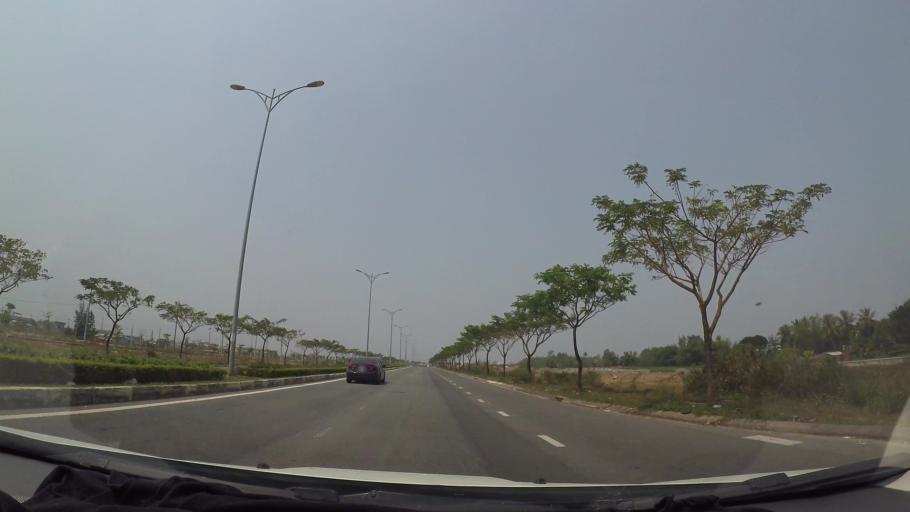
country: VN
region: Da Nang
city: Ngu Hanh Son
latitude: 15.9893
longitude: 108.2388
